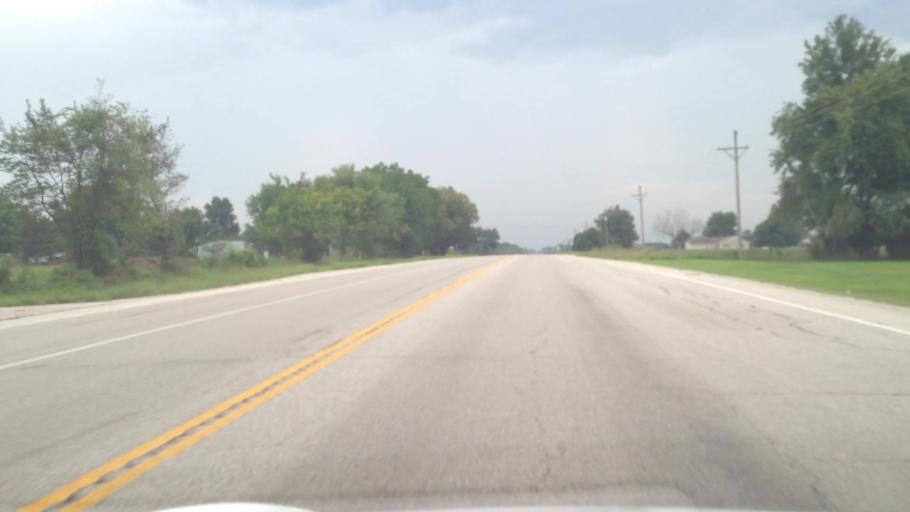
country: US
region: Kansas
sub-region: Cherokee County
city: Galena
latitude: 37.1040
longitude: -94.7044
